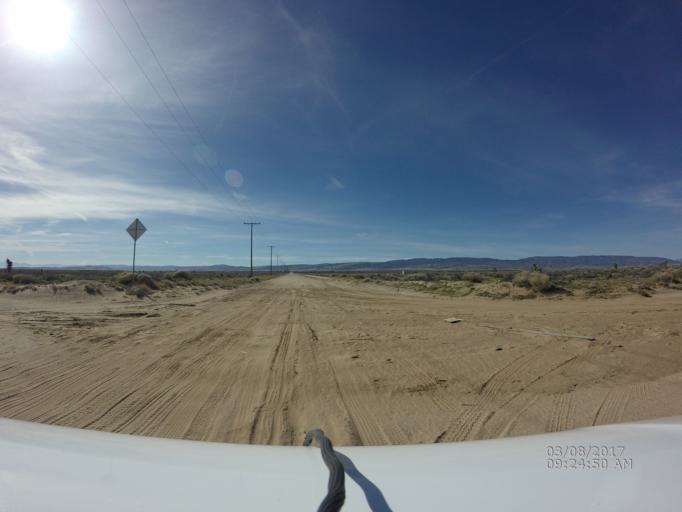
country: US
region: California
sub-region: Los Angeles County
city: Green Valley
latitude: 34.8183
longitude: -118.4670
